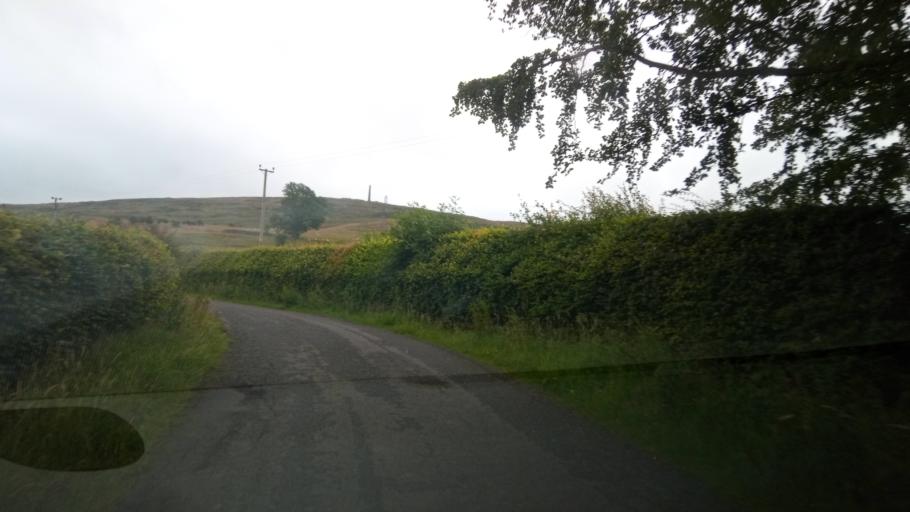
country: GB
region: Scotland
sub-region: Dumfries and Galloway
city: Langholm
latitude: 55.1561
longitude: -2.9908
